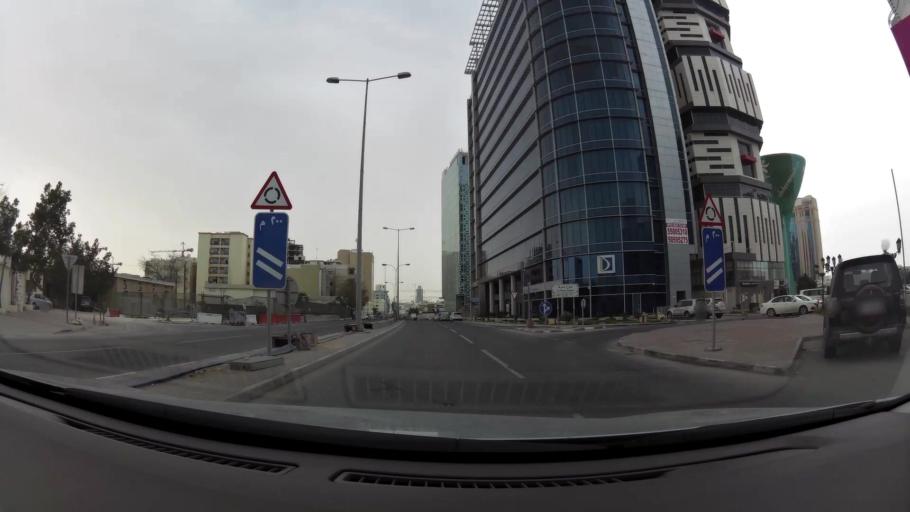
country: QA
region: Baladiyat ad Dawhah
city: Doha
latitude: 25.2868
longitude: 51.5423
